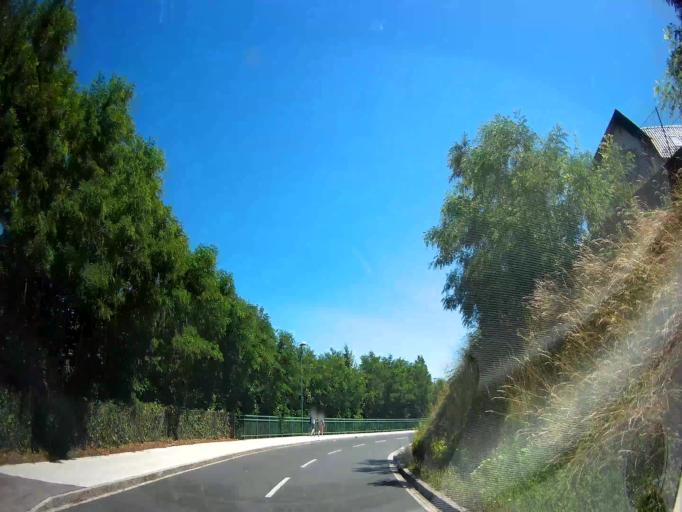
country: AT
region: Carinthia
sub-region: Politischer Bezirk Klagenfurt Land
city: Maria Worth
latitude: 46.6136
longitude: 14.1667
